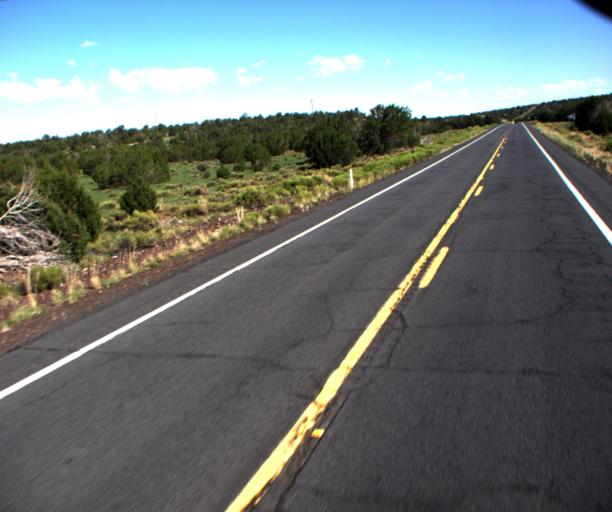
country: US
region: Arizona
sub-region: Coconino County
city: Williams
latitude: 35.4582
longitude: -112.1707
